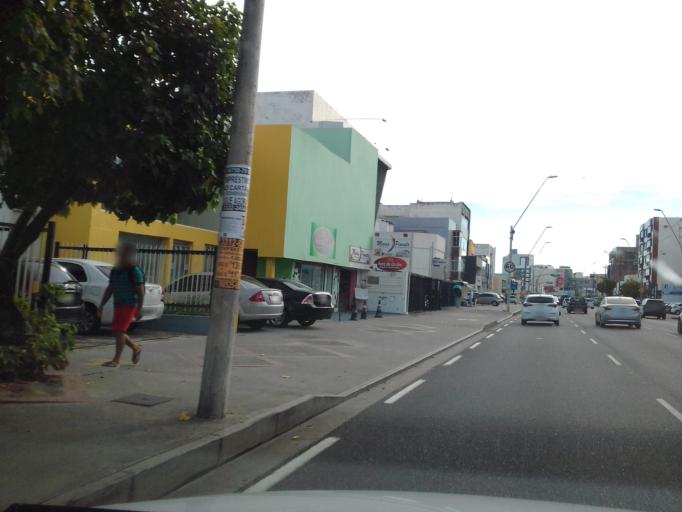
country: BR
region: Bahia
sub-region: Salvador
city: Salvador
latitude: -13.0096
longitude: -38.4656
